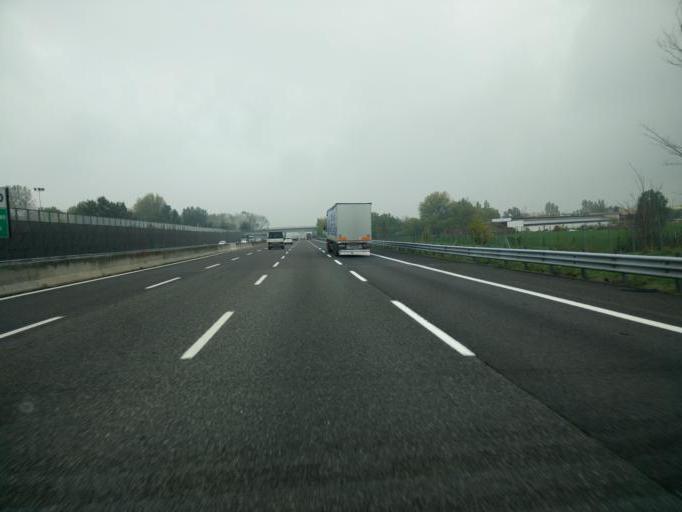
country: IT
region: Emilia-Romagna
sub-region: Provincia di Modena
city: Baggiovara
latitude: 44.6336
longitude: 10.8755
